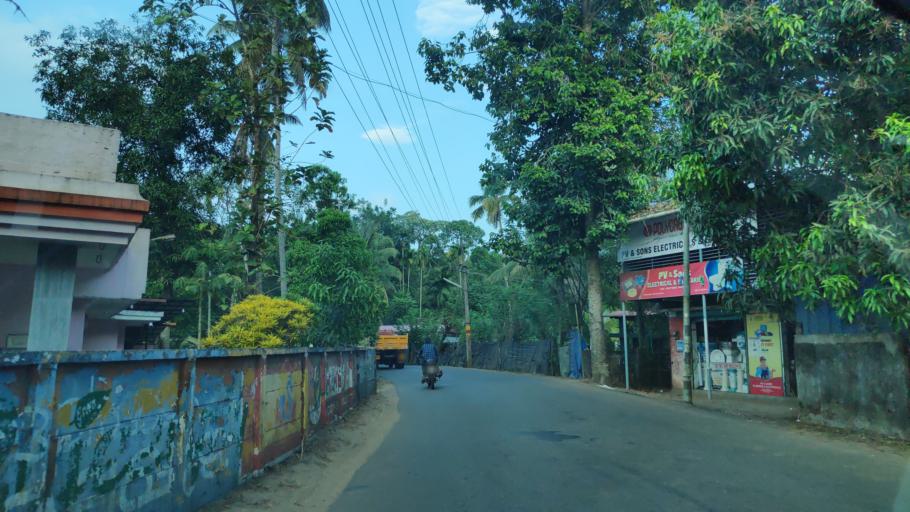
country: IN
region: Kerala
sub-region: Alappuzha
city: Shertallai
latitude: 9.6690
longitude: 76.3884
